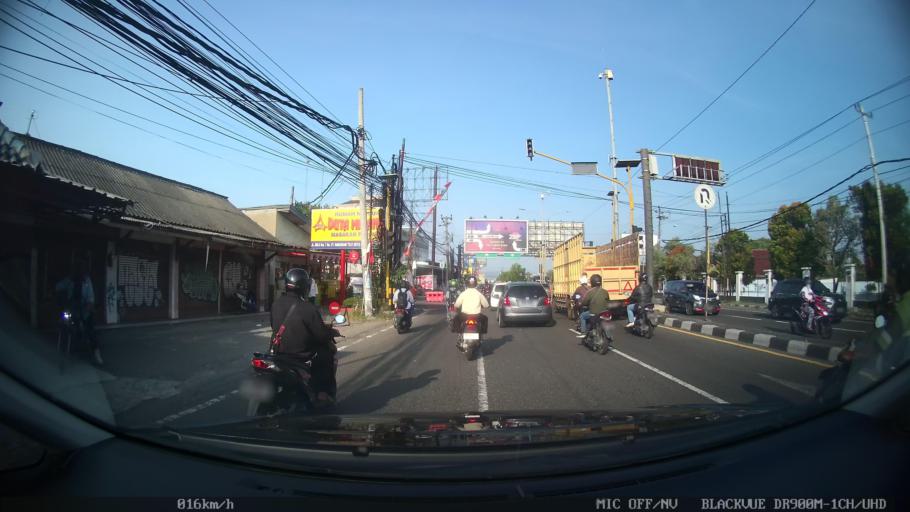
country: ID
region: Daerah Istimewa Yogyakarta
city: Depok
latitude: -7.7841
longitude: 110.4133
